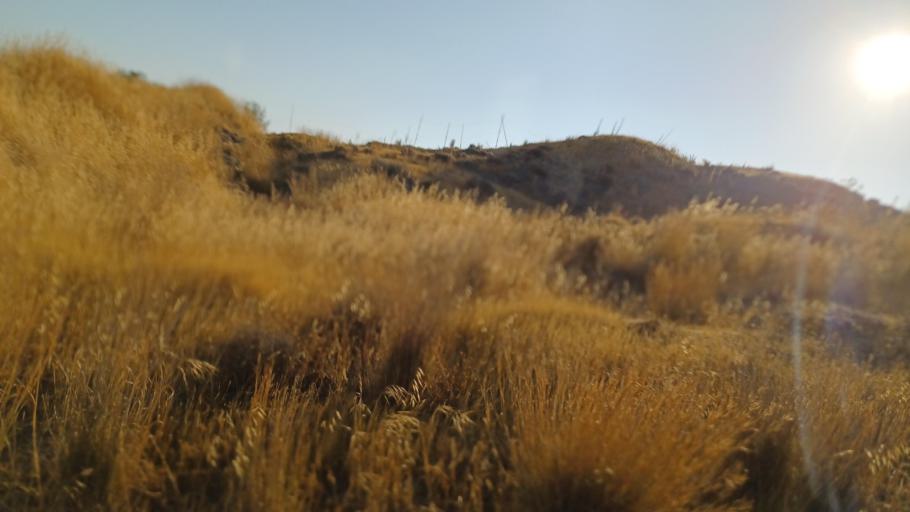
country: CY
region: Larnaka
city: Troulloi
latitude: 35.0142
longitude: 33.5924
